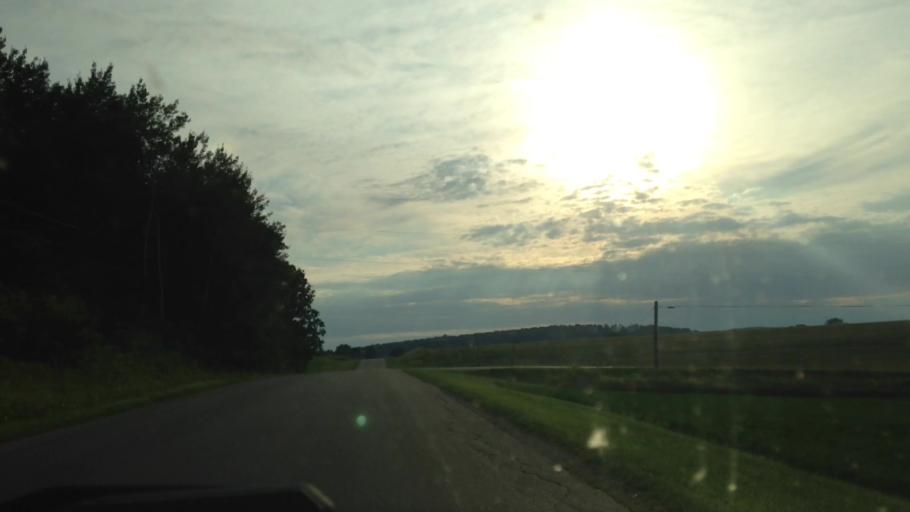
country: US
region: Wisconsin
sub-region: Dodge County
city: Theresa
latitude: 43.4860
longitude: -88.4791
